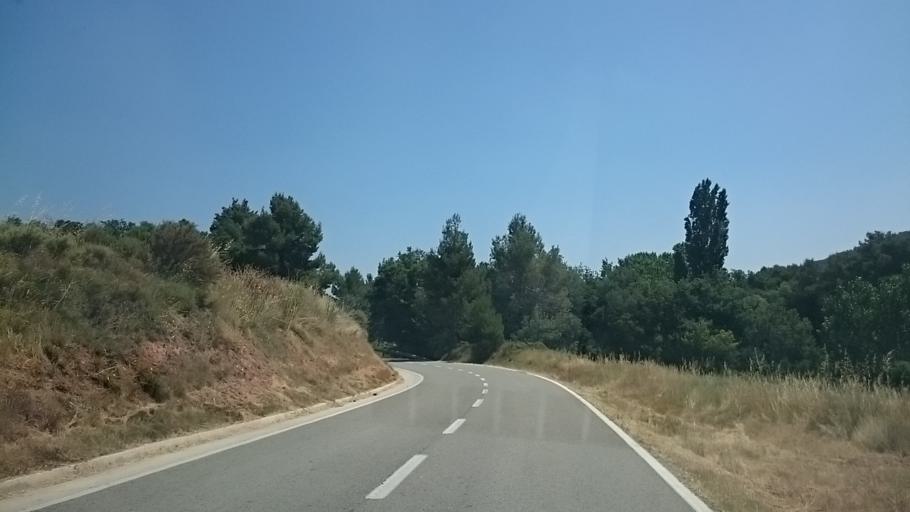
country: ES
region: Catalonia
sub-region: Provincia de Barcelona
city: Bellprat
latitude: 41.4790
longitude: 1.4938
